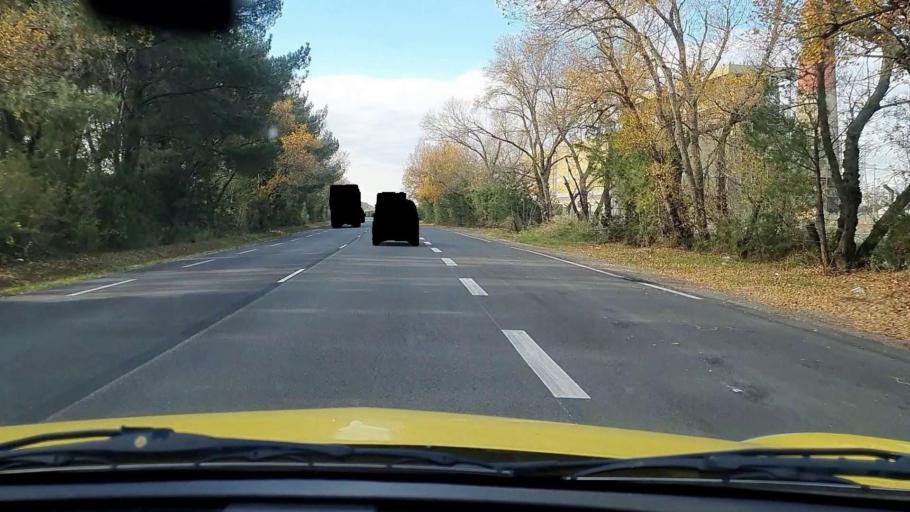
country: FR
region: Languedoc-Roussillon
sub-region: Departement du Gard
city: Aramon
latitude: 43.8816
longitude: 4.6633
